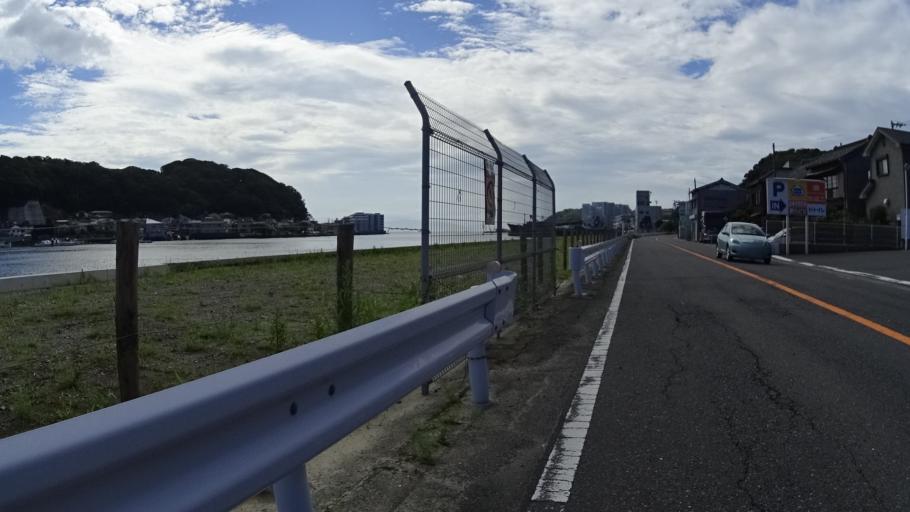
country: JP
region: Kanagawa
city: Yokosuka
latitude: 35.2434
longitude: 139.7181
